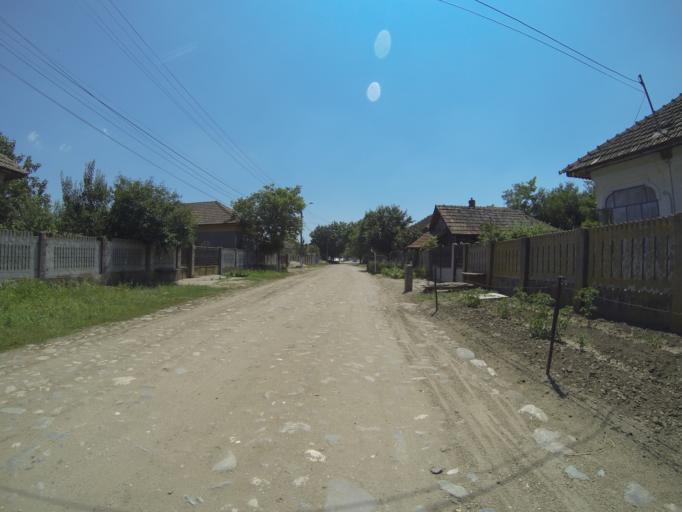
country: RO
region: Dolj
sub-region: Comuna Segarcea
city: Segarcea
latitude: 44.0897
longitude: 23.7406
